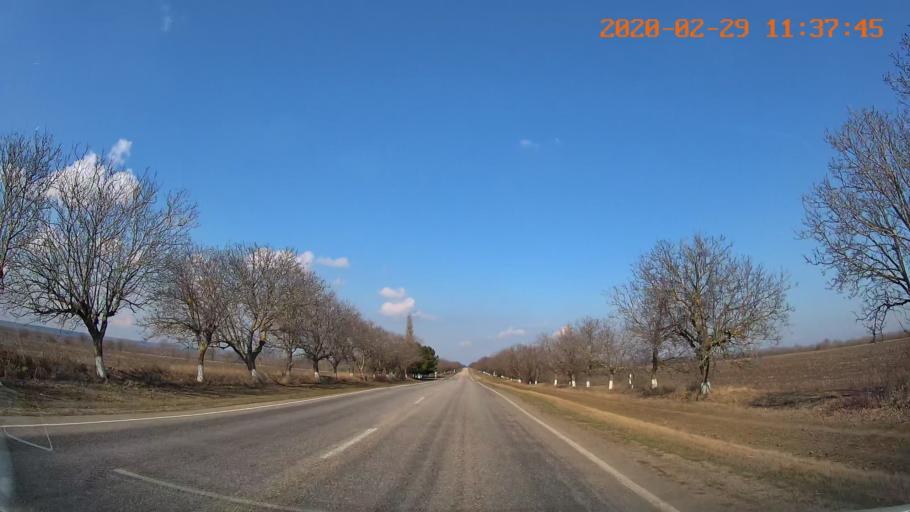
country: MD
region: Rezina
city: Saharna
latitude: 47.6160
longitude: 29.0432
